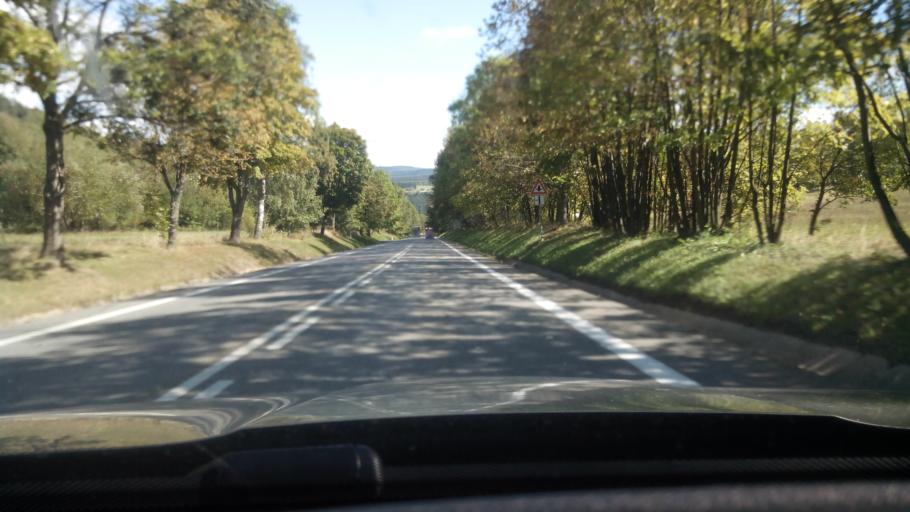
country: CZ
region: Jihocesky
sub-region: Okres Prachatice
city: Vimperk
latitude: 49.0608
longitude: 13.7619
